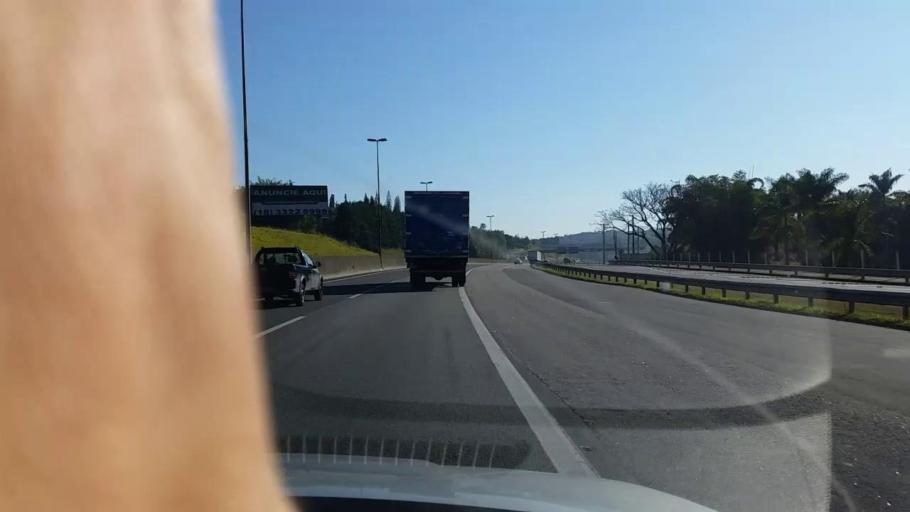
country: BR
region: Sao Paulo
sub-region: Varzea Paulista
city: Varzea Paulista
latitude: -23.2571
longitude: -46.8673
